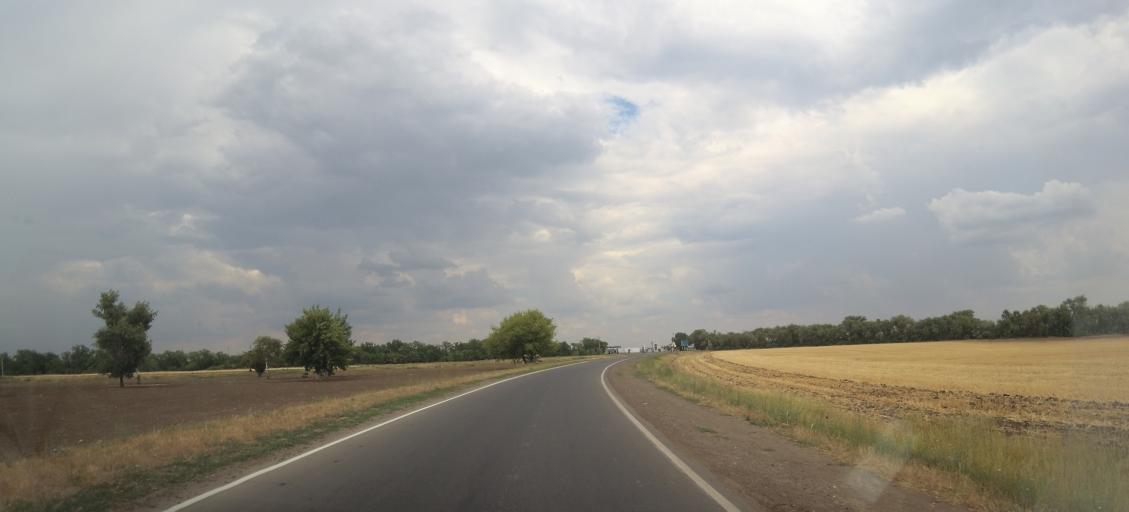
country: RU
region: Rostov
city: Sal'sk
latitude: 46.4723
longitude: 41.4754
